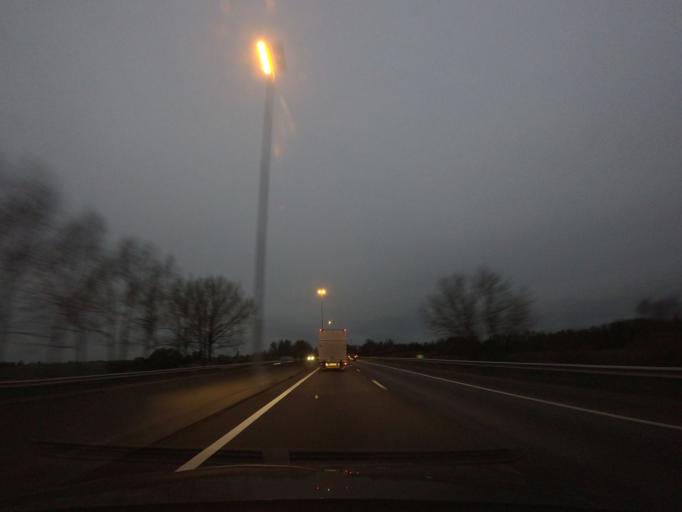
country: NL
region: Utrecht
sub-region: Gemeente Lopik
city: Lopik
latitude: 51.9361
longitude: 5.0004
